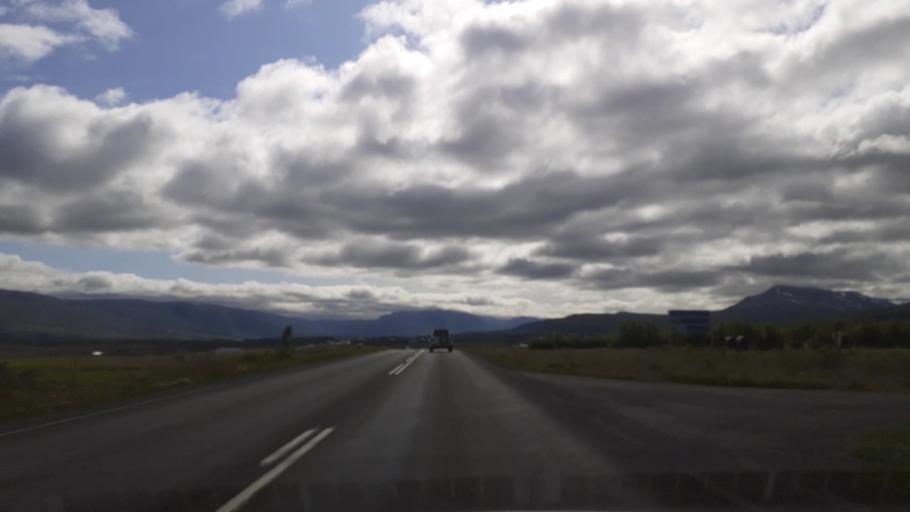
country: IS
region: Northeast
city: Akureyri
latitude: 65.7236
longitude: -18.1807
